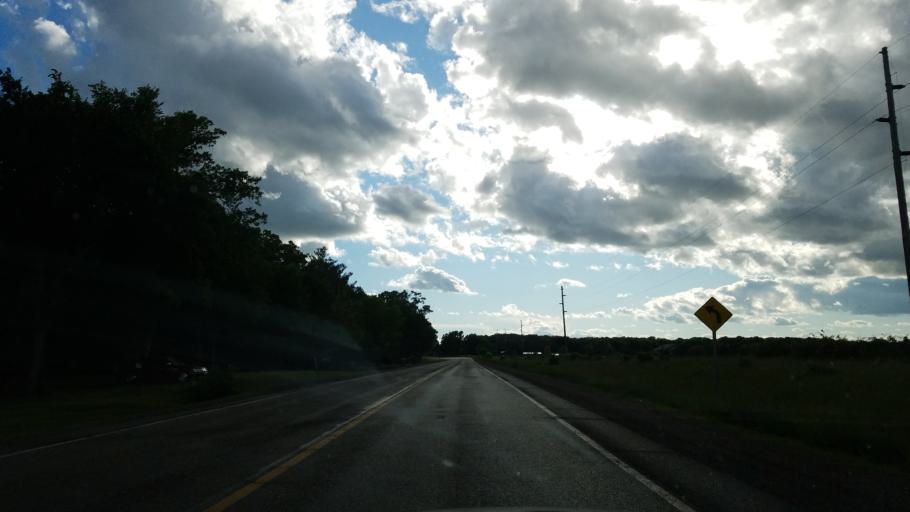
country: US
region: Wisconsin
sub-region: Polk County
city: Osceola
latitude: 45.3433
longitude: -92.6607
